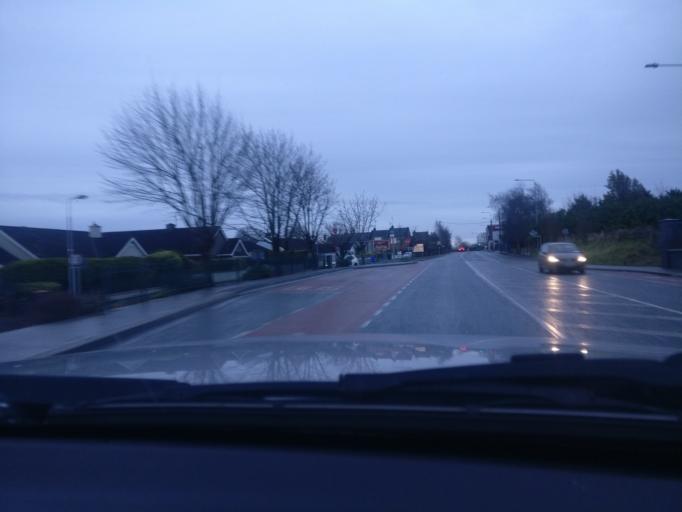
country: IE
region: Leinster
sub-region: An Mhi
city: Kells
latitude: 53.7308
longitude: -6.8850
